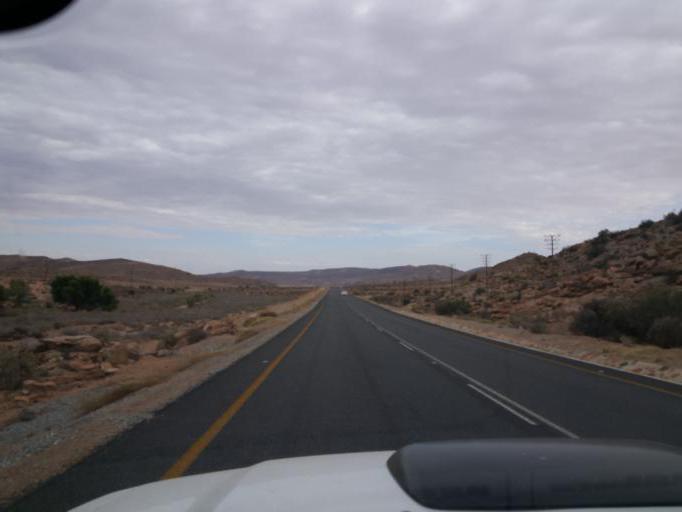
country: ZA
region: Northern Cape
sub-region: Namakwa District Municipality
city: Springbok
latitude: -29.5026
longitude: 17.8462
